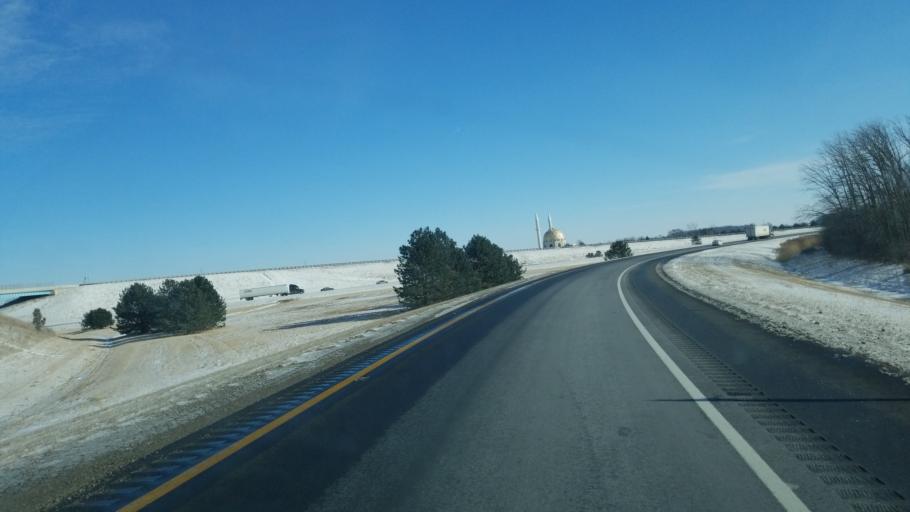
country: US
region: Ohio
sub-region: Wood County
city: Perrysburg
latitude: 41.5312
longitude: -83.6249
